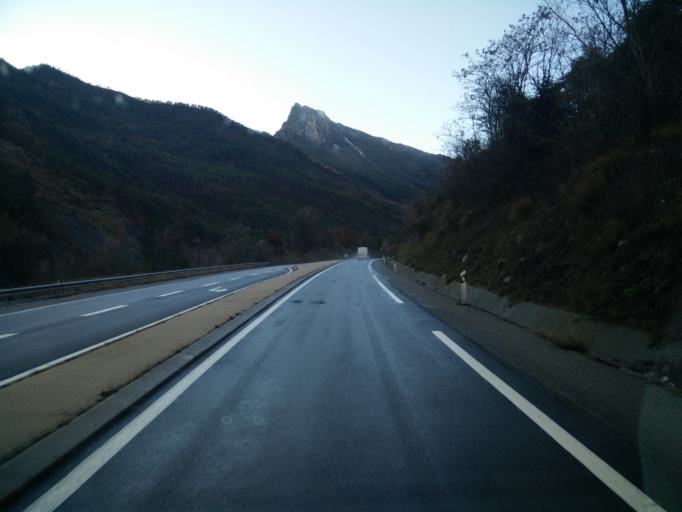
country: FR
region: Provence-Alpes-Cote d'Azur
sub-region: Departement des Alpes-Maritimes
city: Puget-Theniers
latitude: 43.9495
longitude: 6.9801
